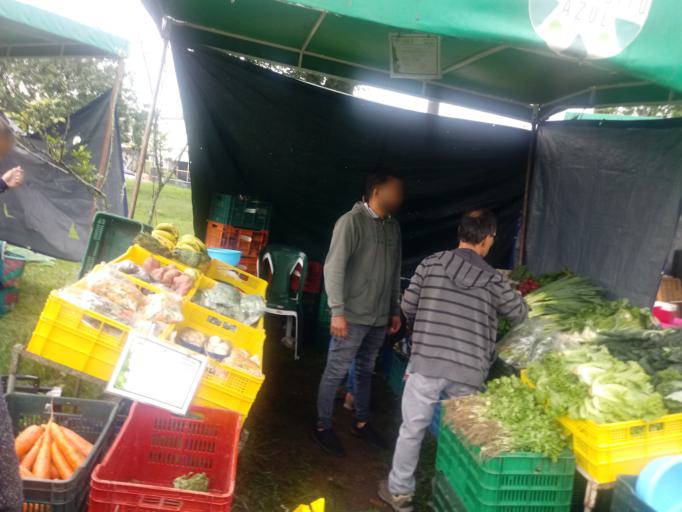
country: CR
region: Cartago
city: Cartago
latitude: 9.8574
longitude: -83.9278
